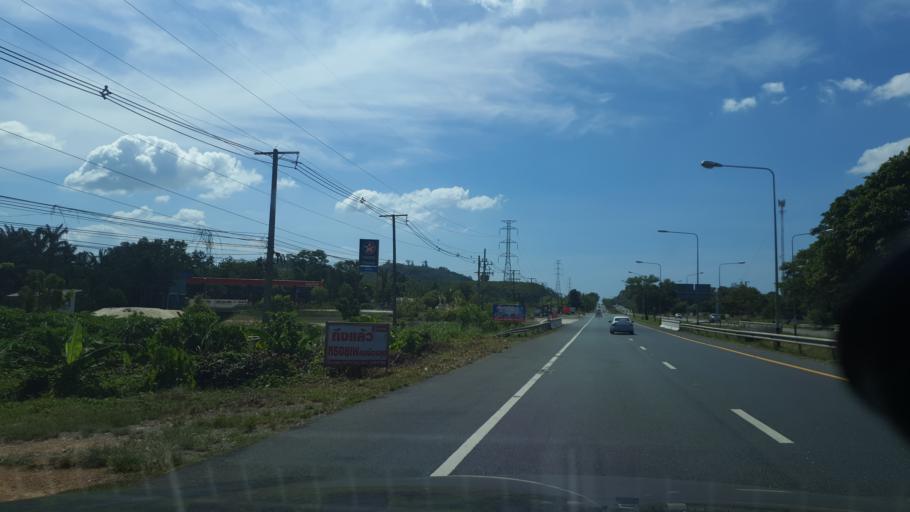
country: TH
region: Phangnga
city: Thai Mueang
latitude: 8.2690
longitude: 98.3342
